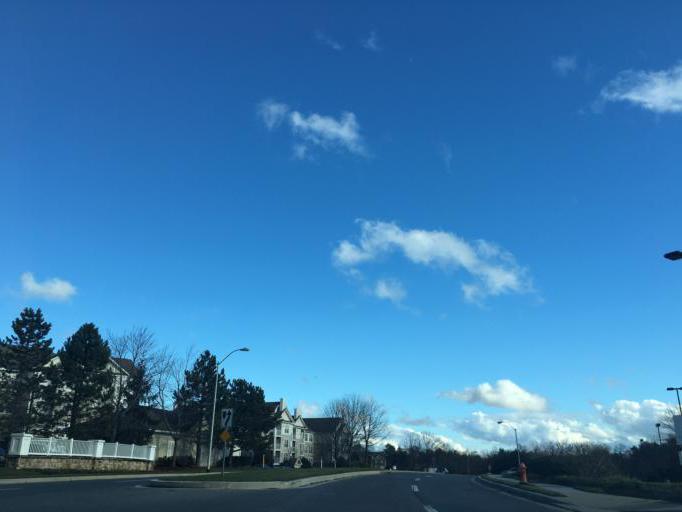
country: US
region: Maryland
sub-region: Baltimore County
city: Owings Mills
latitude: 39.3989
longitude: -76.7920
